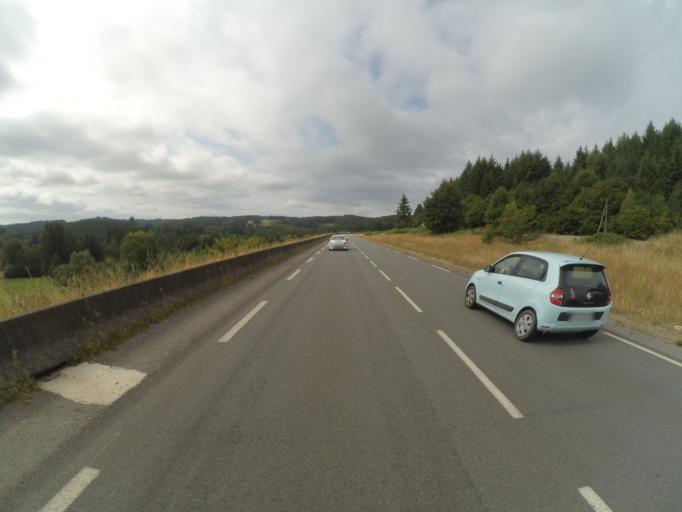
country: FR
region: Limousin
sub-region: Departement de la Correze
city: Ussel
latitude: 45.5242
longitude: 2.2921
